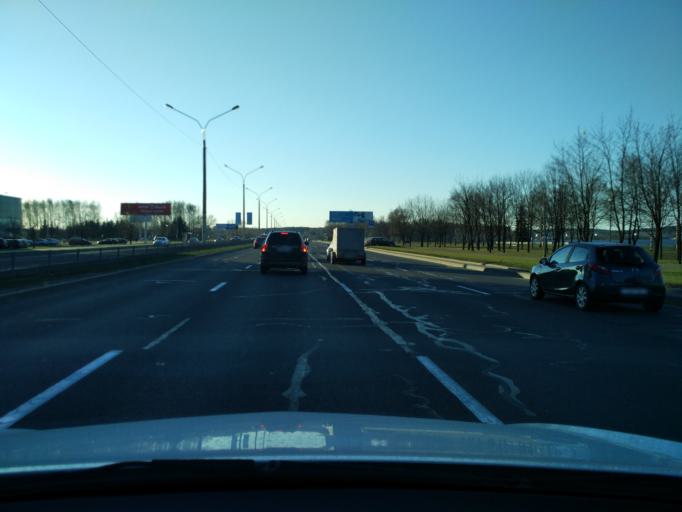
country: BY
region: Minsk
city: Zhdanovichy
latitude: 53.9432
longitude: 27.4639
